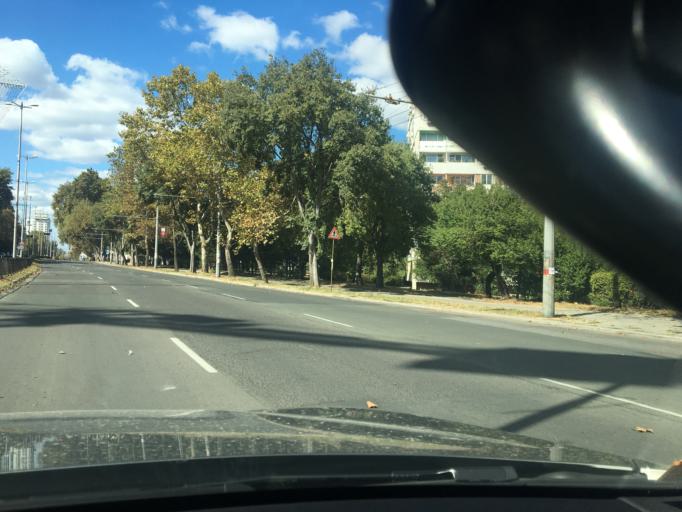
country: BG
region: Burgas
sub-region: Obshtina Burgas
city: Burgas
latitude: 42.5047
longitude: 27.4738
